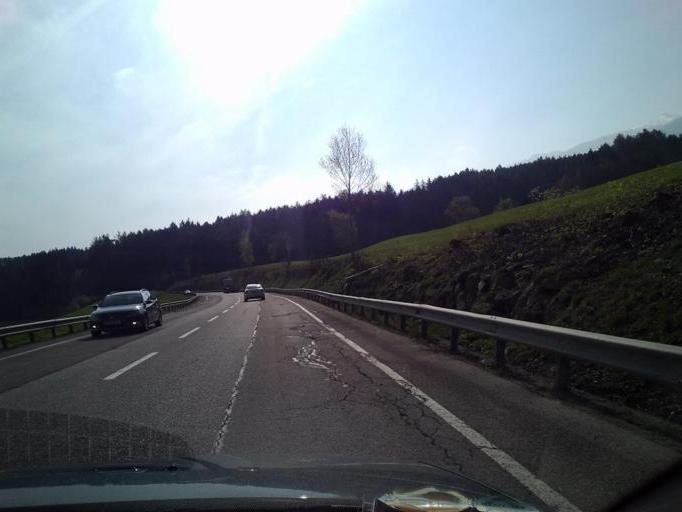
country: IT
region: Trentino-Alto Adige
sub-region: Bolzano
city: San Lorenzo di Sebato
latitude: 46.7804
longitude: 11.9177
